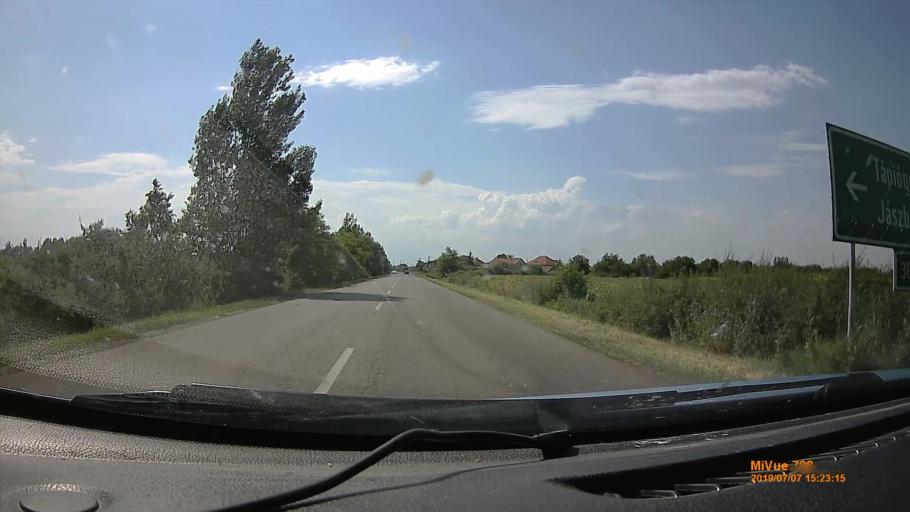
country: HU
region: Jasz-Nagykun-Szolnok
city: Janoshida
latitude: 47.3867
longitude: 20.0669
